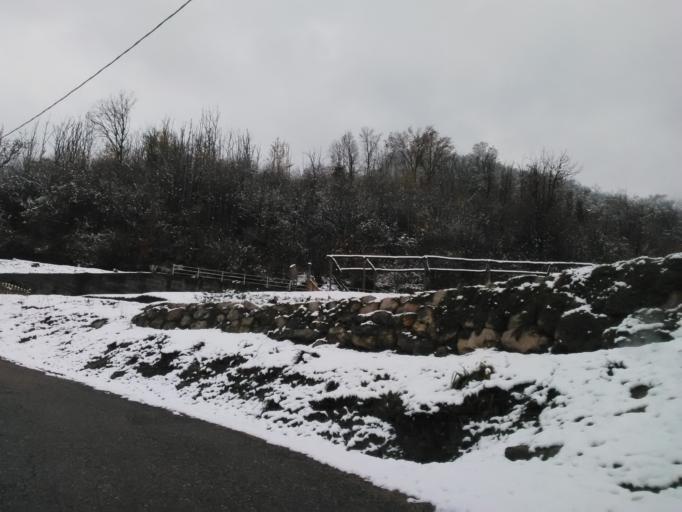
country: IT
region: Piedmont
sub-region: Provincia di Vercelli
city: Varallo
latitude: 45.7865
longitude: 8.2524
